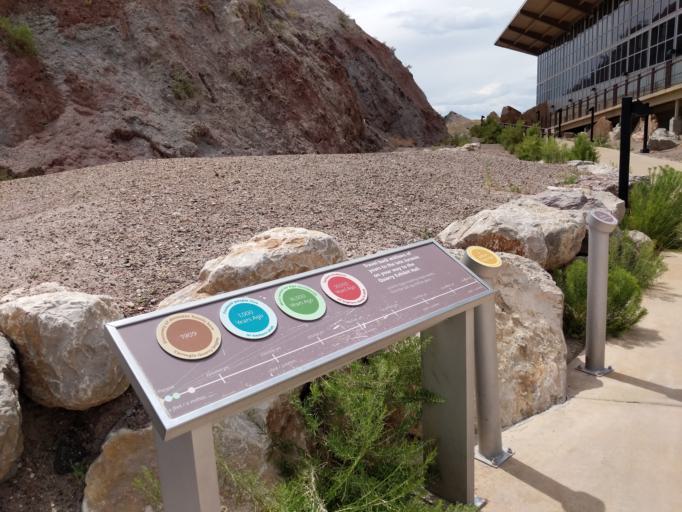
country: US
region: Utah
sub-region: Uintah County
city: Naples
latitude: 40.4403
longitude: -109.3010
